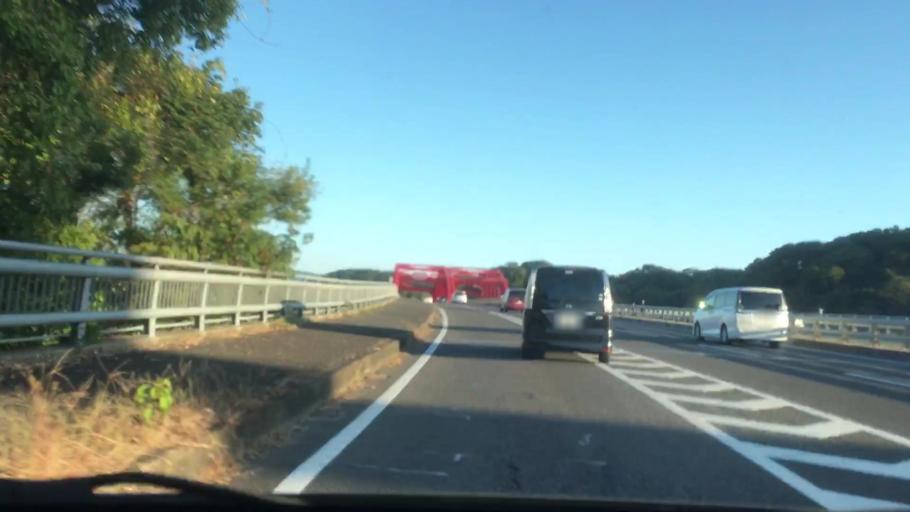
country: JP
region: Nagasaki
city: Sasebo
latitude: 33.1439
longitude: 129.7800
